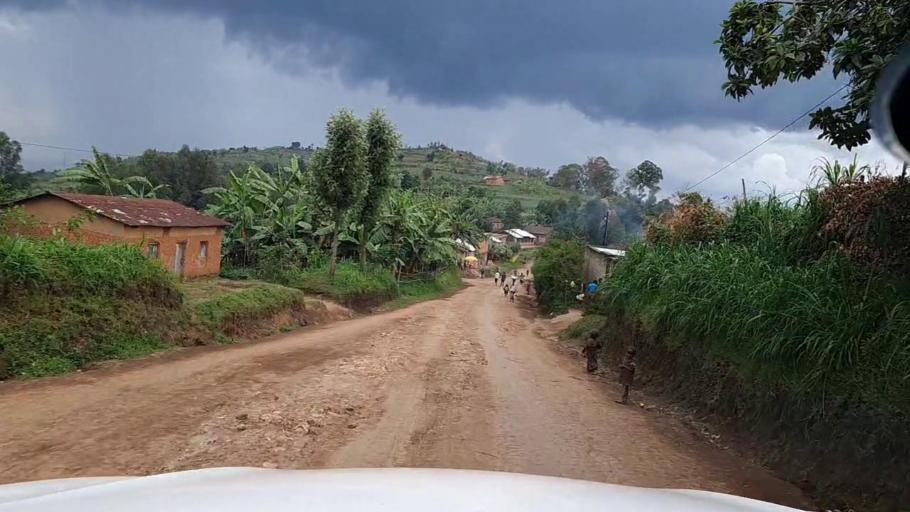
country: BI
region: Kayanza
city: Kayanza
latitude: -2.7913
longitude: 29.5191
